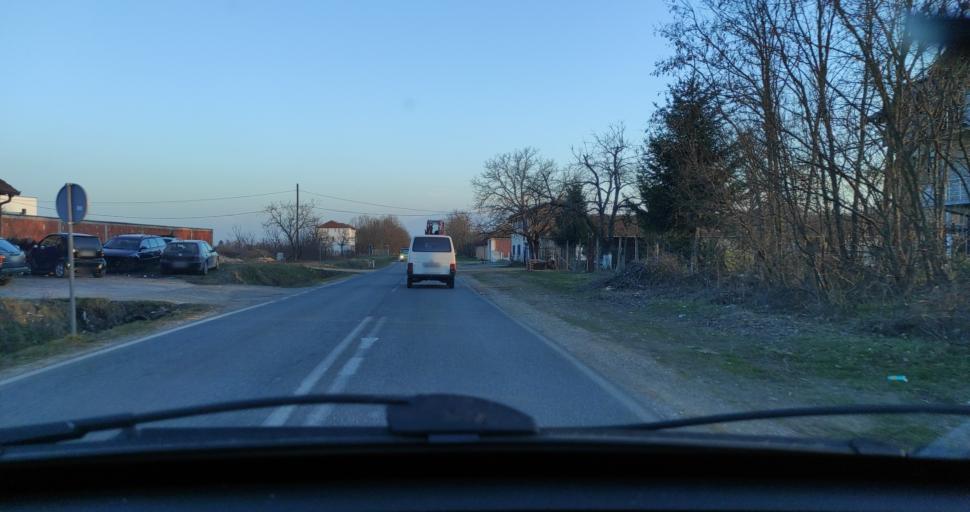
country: XK
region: Gjakova
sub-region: Komuna e Decanit
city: Gllogjan
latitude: 42.4429
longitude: 20.3660
